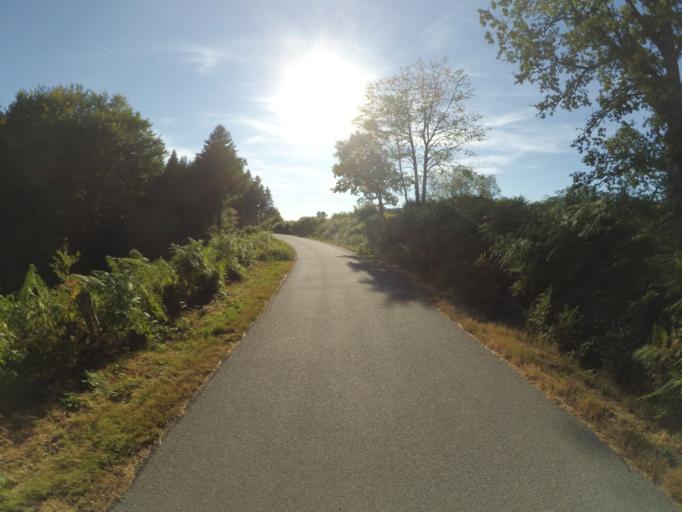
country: FR
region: Limousin
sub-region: Departement de la Creuse
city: Banize
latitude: 45.7705
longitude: 2.0064
